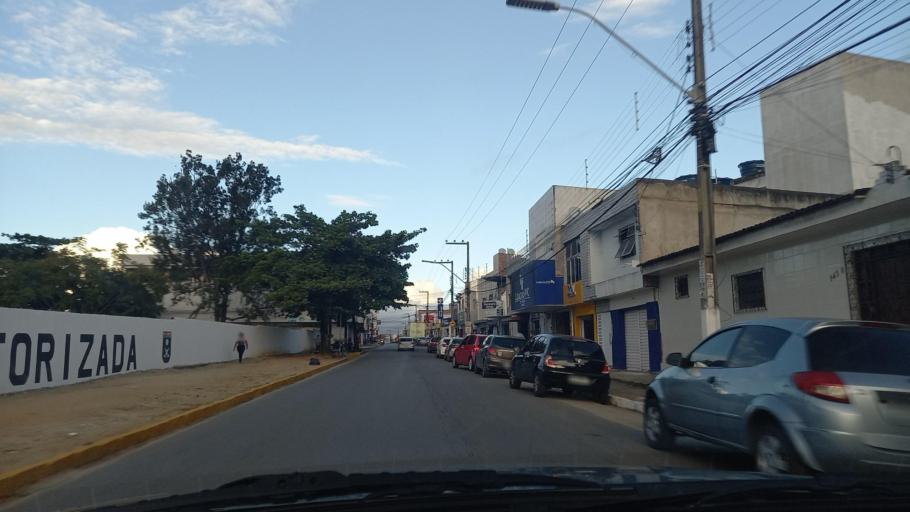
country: BR
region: Pernambuco
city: Garanhuns
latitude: -8.8843
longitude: -36.4705
